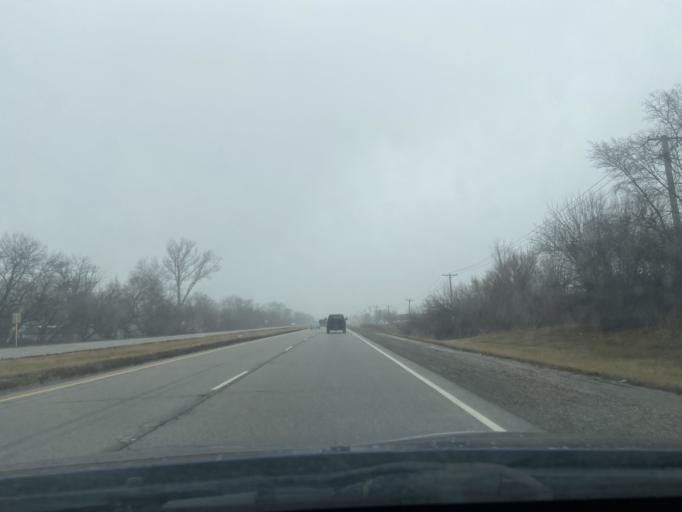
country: US
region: Illinois
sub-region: Lake County
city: Wauconda
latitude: 42.2706
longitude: -88.1545
